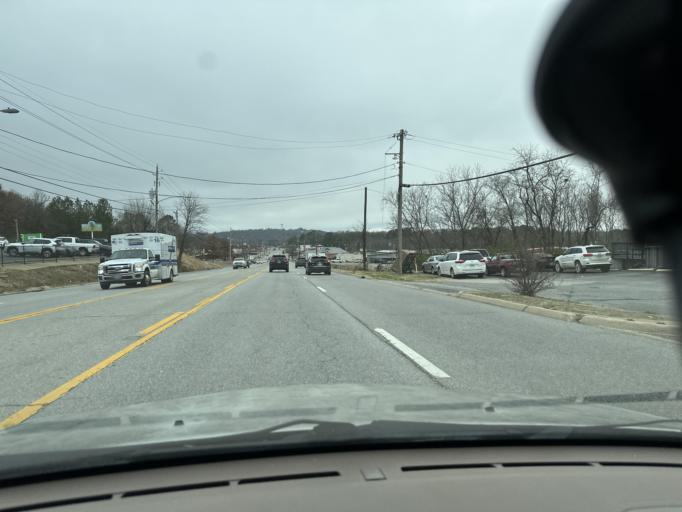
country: US
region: Arkansas
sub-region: Washington County
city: Johnson
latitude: 36.1011
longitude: -94.1495
